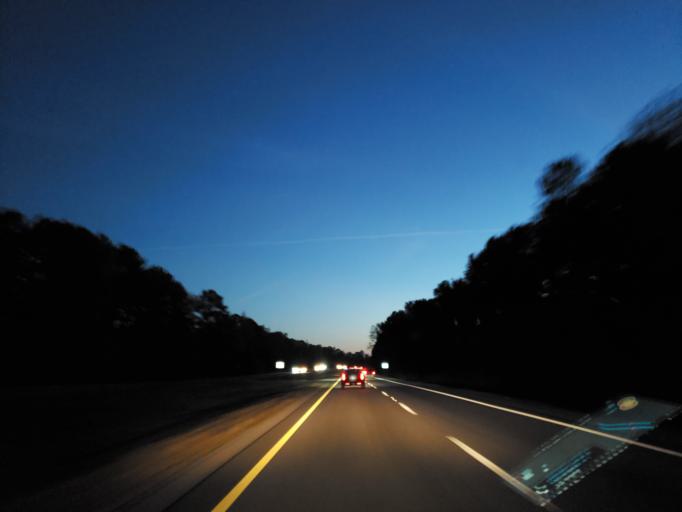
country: US
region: Mississippi
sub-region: Clarke County
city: Stonewall
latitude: 32.2262
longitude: -88.8329
